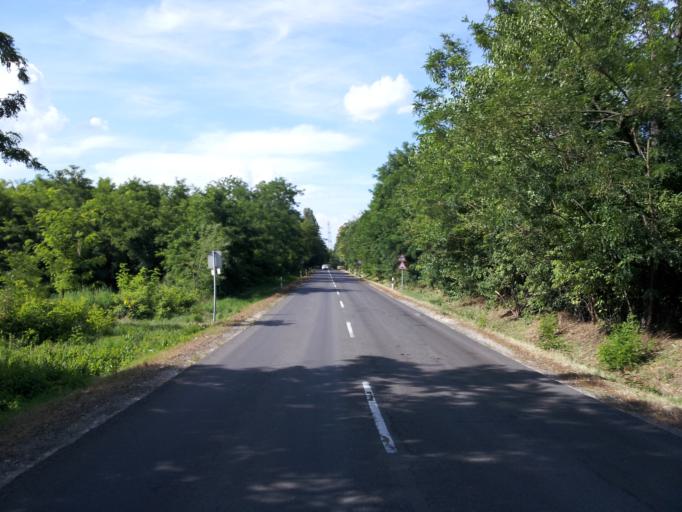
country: HU
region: Pest
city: Kiskunlachaza
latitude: 47.2382
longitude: 19.0207
